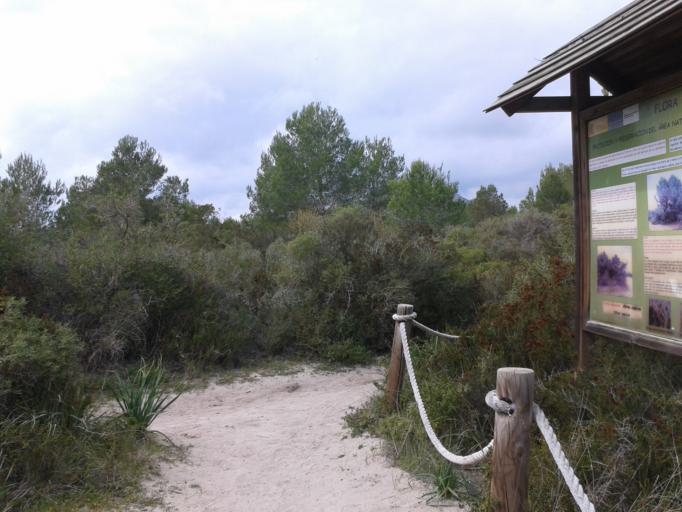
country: ES
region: Balearic Islands
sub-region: Illes Balears
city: Son Servera
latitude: 39.5834
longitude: 3.3837
